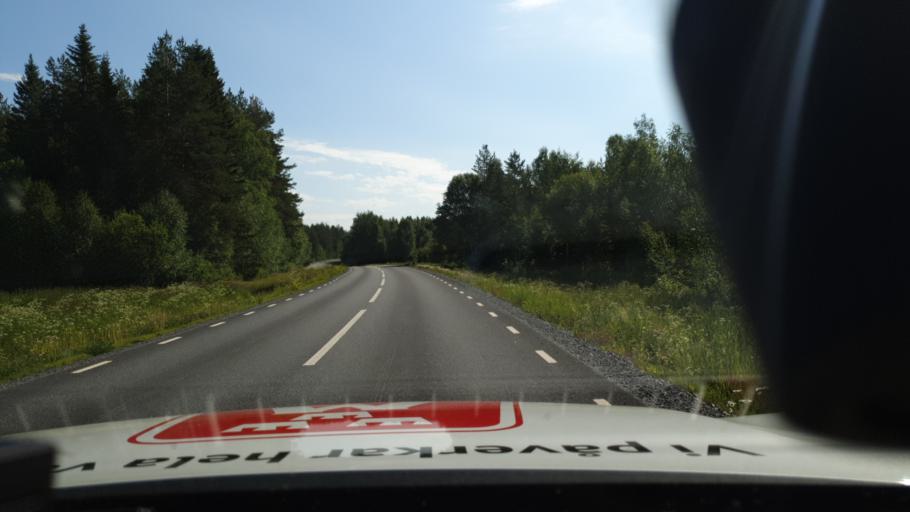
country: SE
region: Norrbotten
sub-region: Bodens Kommun
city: Boden
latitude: 65.8440
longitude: 21.7591
